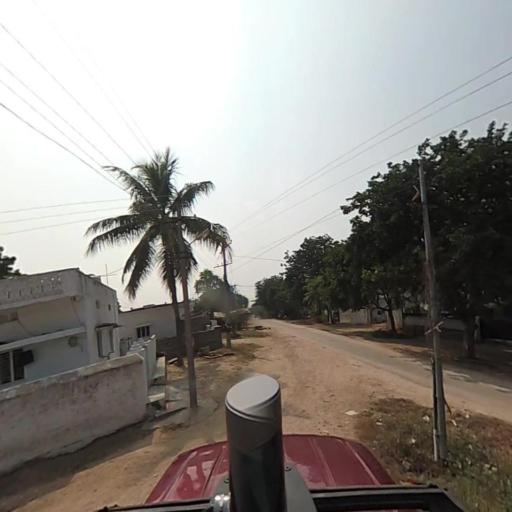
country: IN
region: Telangana
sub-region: Nalgonda
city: Nalgonda
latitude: 17.1909
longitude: 79.1307
